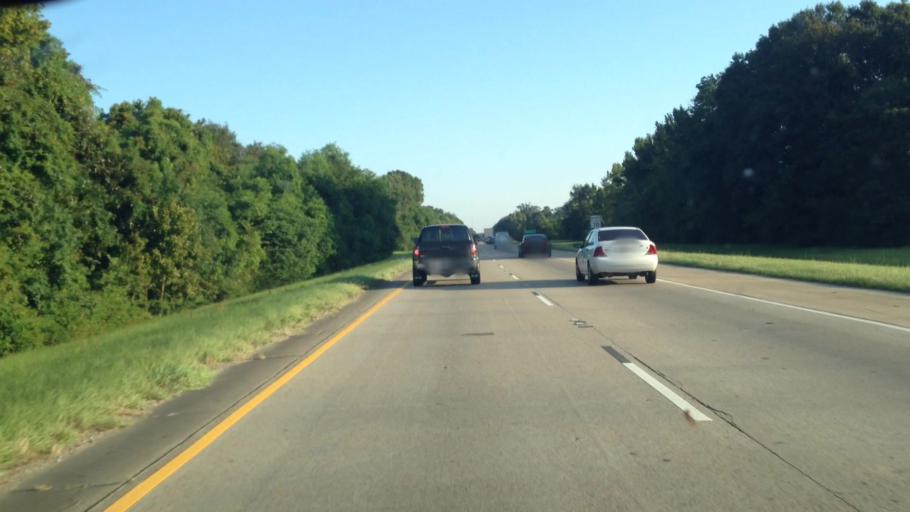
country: US
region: Louisiana
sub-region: Ascension Parish
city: Prairieville
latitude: 30.2806
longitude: -90.9886
